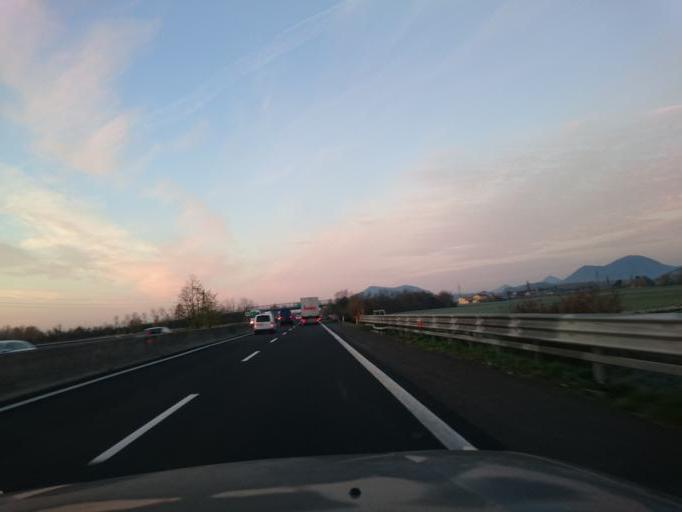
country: IT
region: Veneto
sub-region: Provincia di Padova
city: Carrara San Giorgio
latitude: 45.2994
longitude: 11.8122
